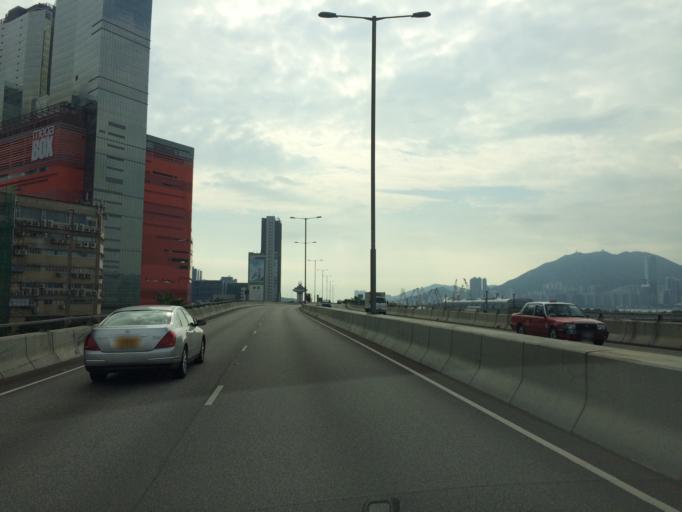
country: HK
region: Kowloon City
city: Kowloon
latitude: 22.3212
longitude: 114.2054
